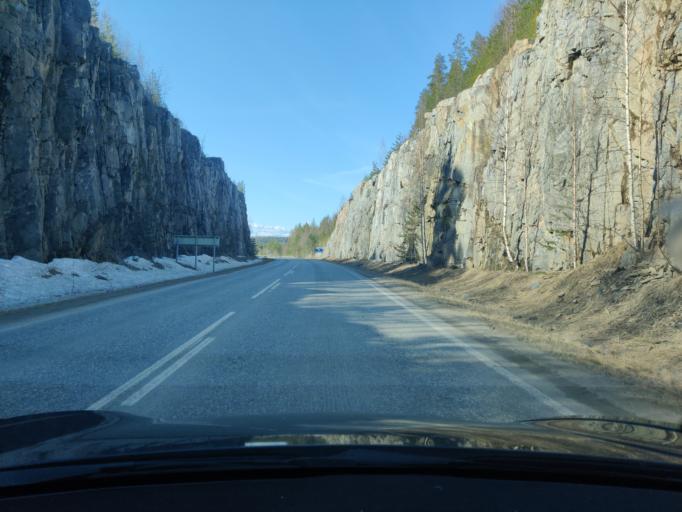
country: FI
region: Northern Savo
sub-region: Kuopio
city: Vehmersalmi
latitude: 62.7726
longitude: 28.0124
